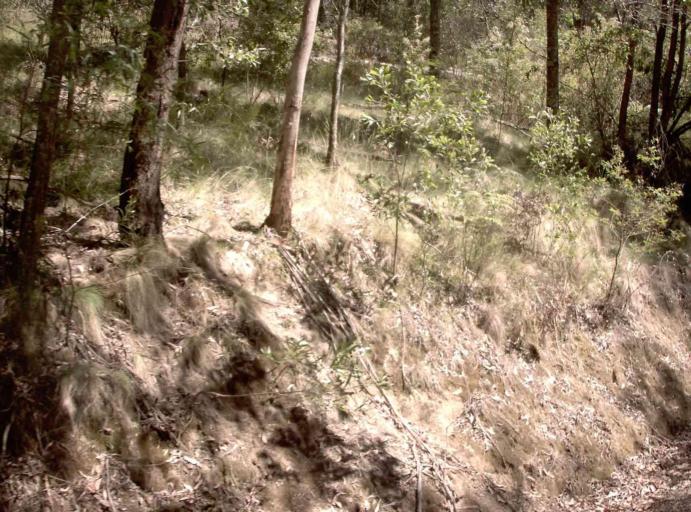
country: AU
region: Victoria
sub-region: East Gippsland
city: Lakes Entrance
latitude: -37.2253
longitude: 148.2637
